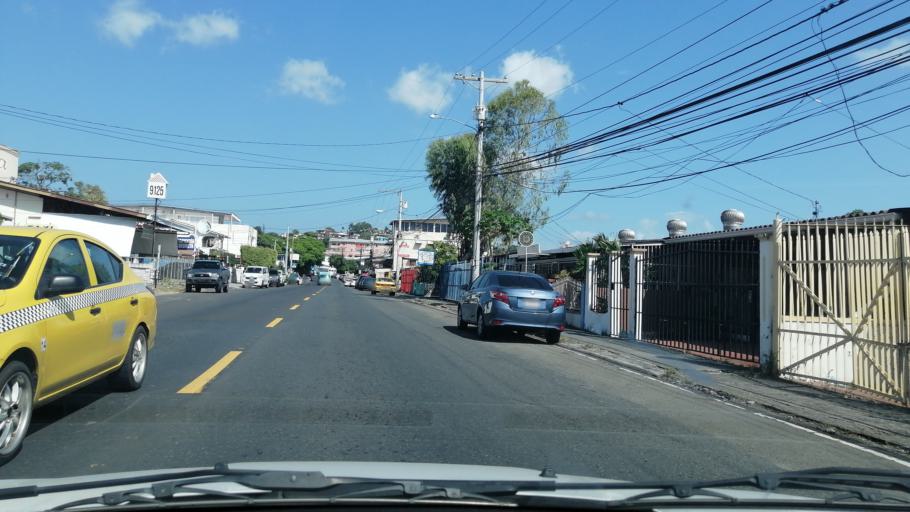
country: PA
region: Panama
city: Panama
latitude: 9.0080
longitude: -79.5234
